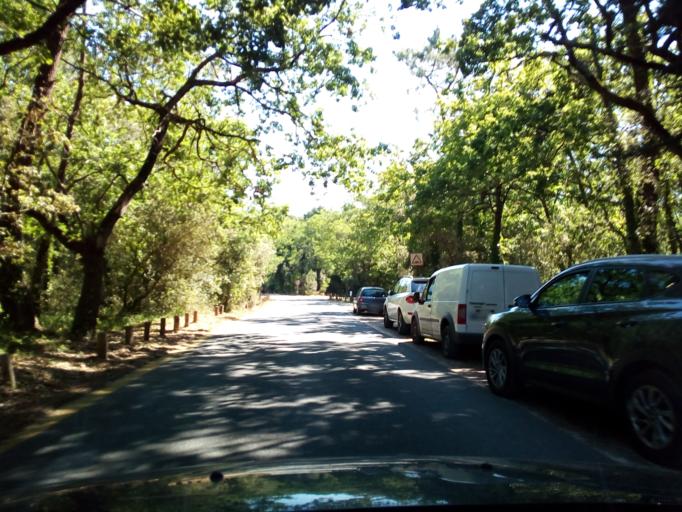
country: FR
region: Poitou-Charentes
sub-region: Departement de la Charente-Maritime
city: Boyard-Ville
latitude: 45.9831
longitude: -1.2947
